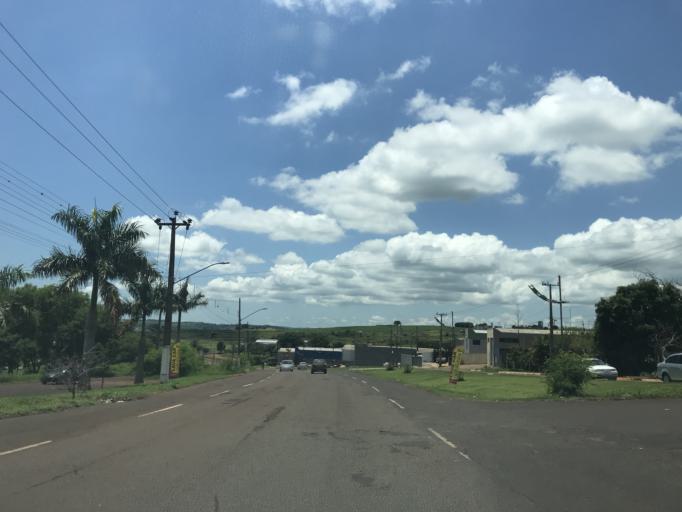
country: BR
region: Parana
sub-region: Marialva
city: Marialva
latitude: -23.4967
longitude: -51.7782
